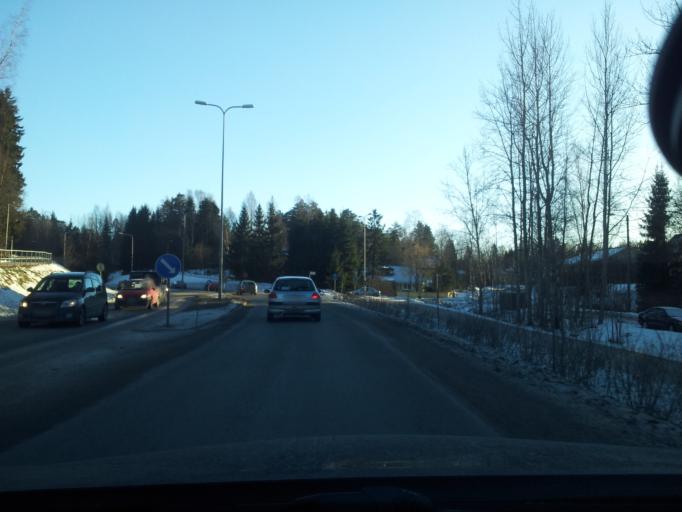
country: FI
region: Uusimaa
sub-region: Helsinki
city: Espoo
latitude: 60.2007
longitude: 24.6528
